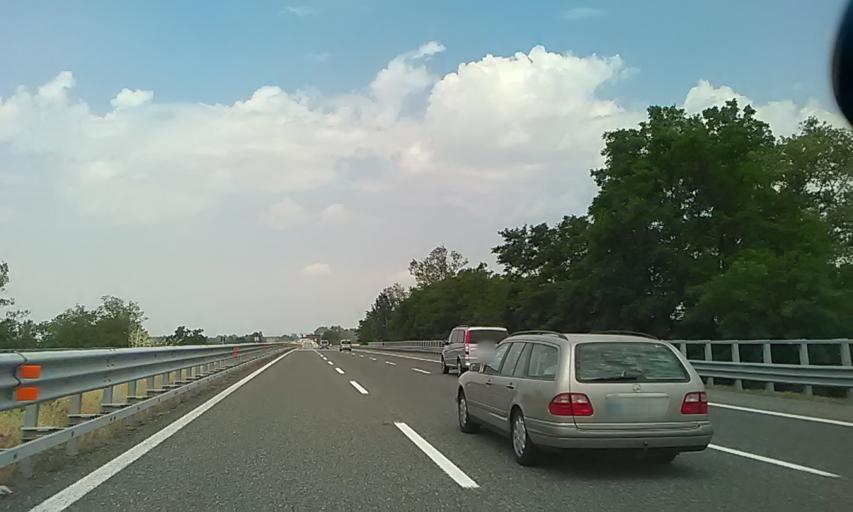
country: IT
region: Piedmont
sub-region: Provincia di Alessandria
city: Castellazzo Bormida
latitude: 44.8508
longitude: 8.5913
